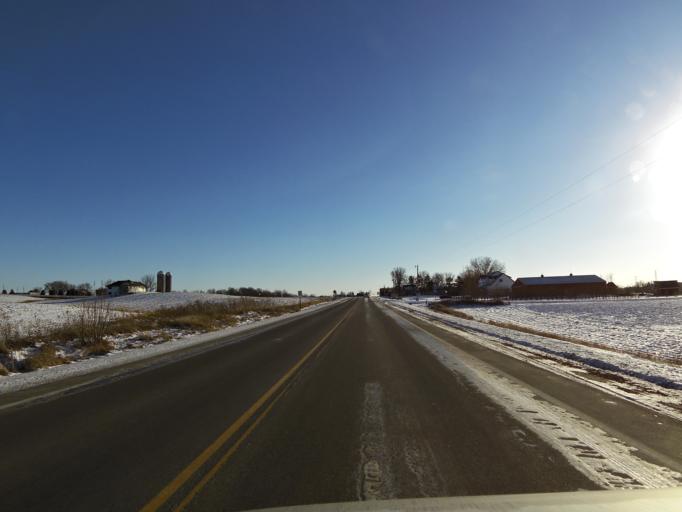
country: US
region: Minnesota
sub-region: Carver County
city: Chaska
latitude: 44.7646
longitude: -93.5612
